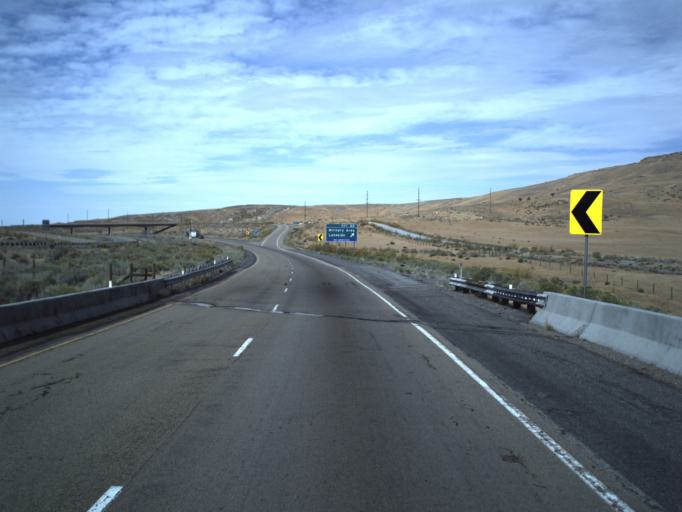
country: US
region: Utah
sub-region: Tooele County
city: Grantsville
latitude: 40.8231
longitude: -112.8966
